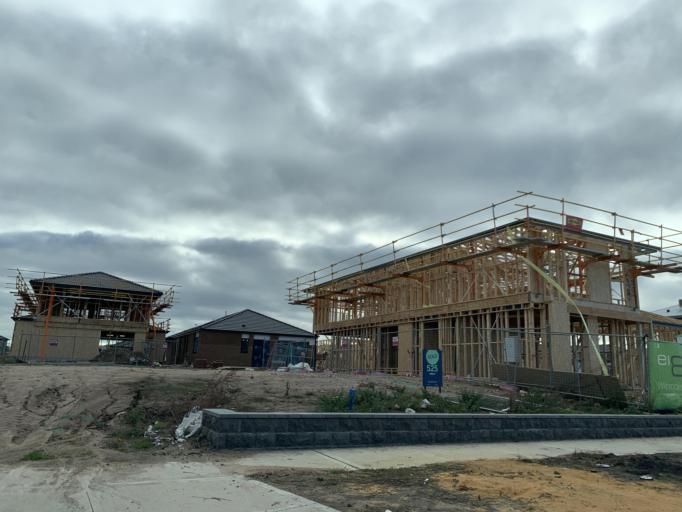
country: AU
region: Victoria
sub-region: Cardinia
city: Officer South
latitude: -38.1241
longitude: 145.3724
